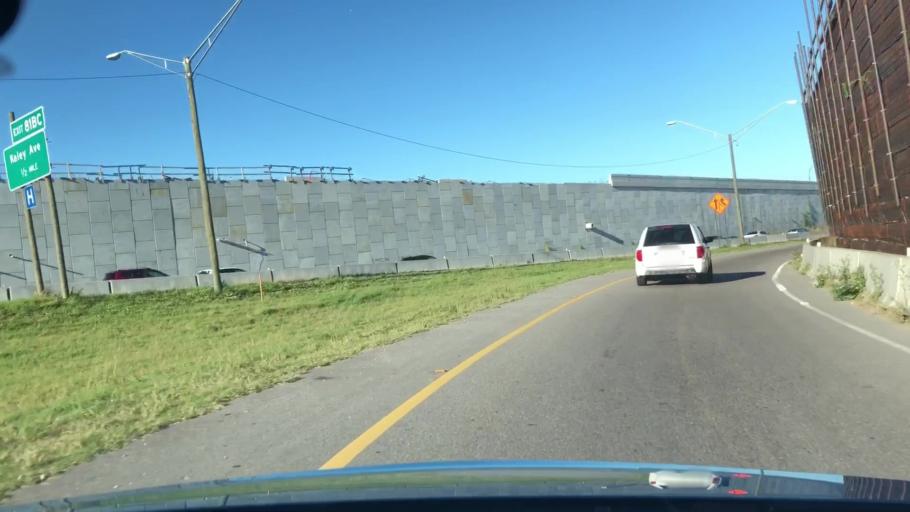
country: US
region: Florida
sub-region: Orange County
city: Holden Heights
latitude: 28.5105
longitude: -81.3954
